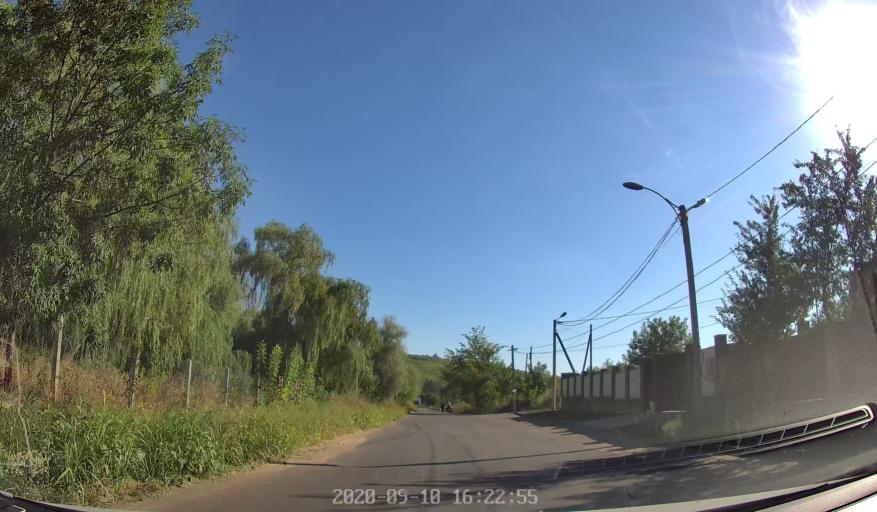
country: MD
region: Chisinau
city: Stauceni
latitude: 47.0509
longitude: 28.9253
